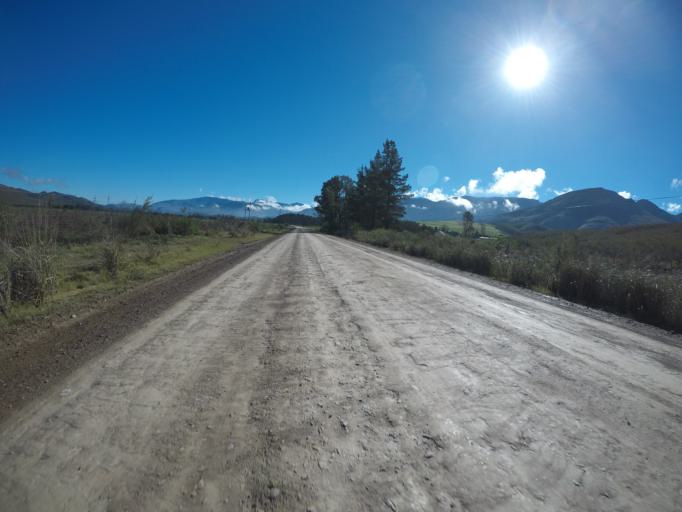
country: ZA
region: Western Cape
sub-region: Overberg District Municipality
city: Caledon
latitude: -34.0749
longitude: 19.6413
